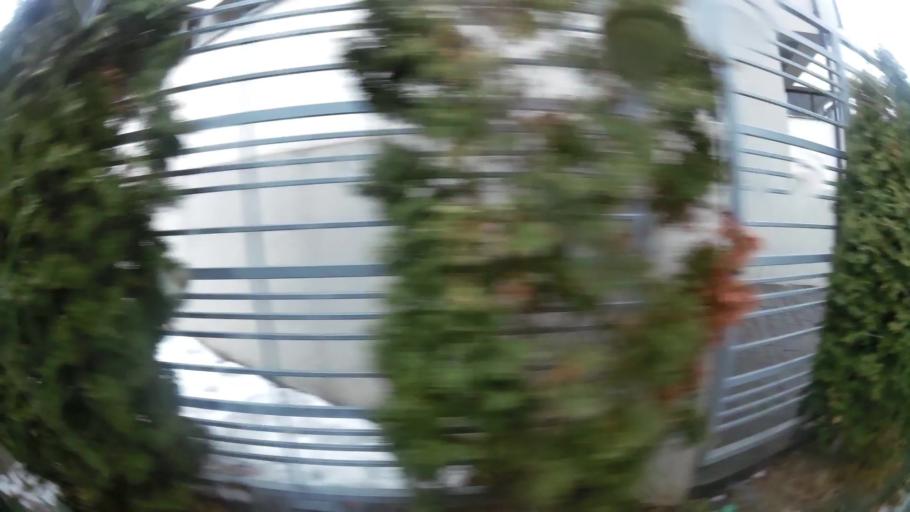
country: RO
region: Ilfov
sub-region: Comuna Chiajna
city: Rosu
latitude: 44.4274
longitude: 26.0128
